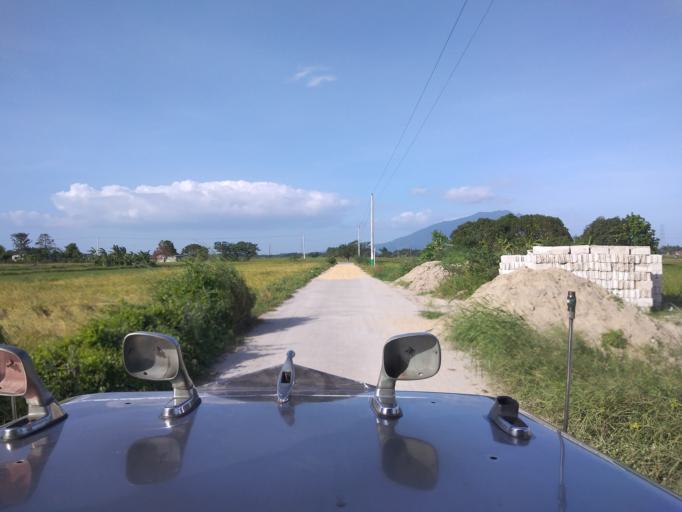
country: PH
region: Central Luzon
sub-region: Province of Pampanga
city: San Patricio
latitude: 15.0987
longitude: 120.6944
